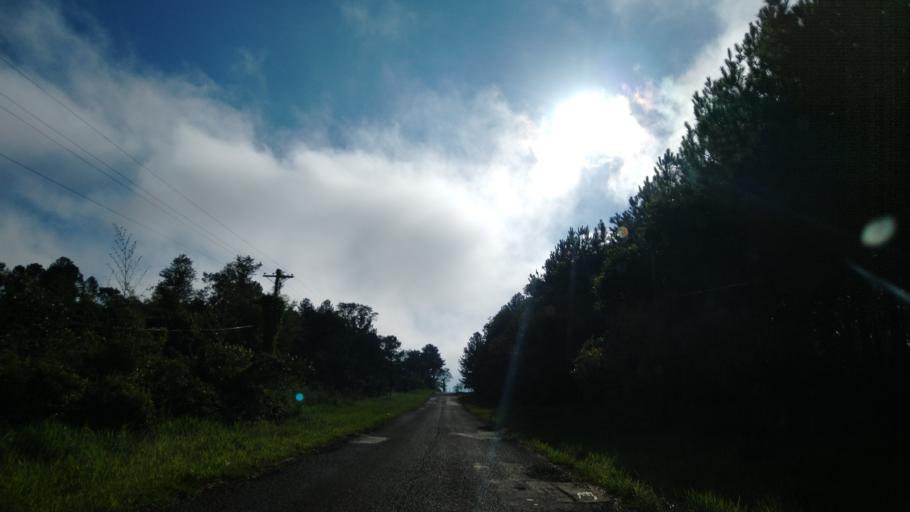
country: AR
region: Misiones
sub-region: Departamento de Montecarlo
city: Montecarlo
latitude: -26.5672
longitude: -54.7952
